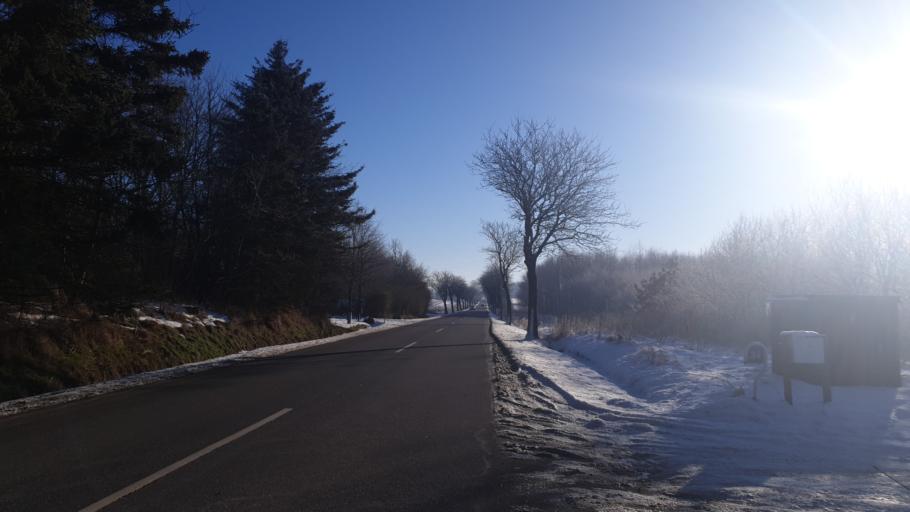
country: DK
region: Central Jutland
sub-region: Hedensted Kommune
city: Hedensted
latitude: 55.8008
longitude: 9.7226
